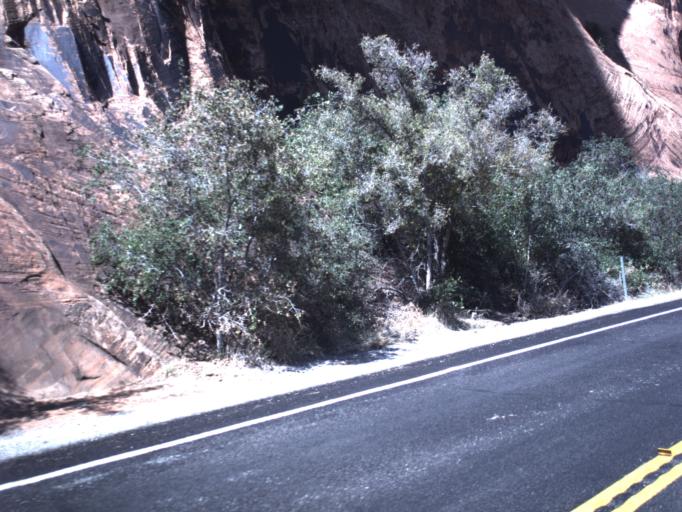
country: US
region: Utah
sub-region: Grand County
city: Moab
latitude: 38.5522
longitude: -109.5951
